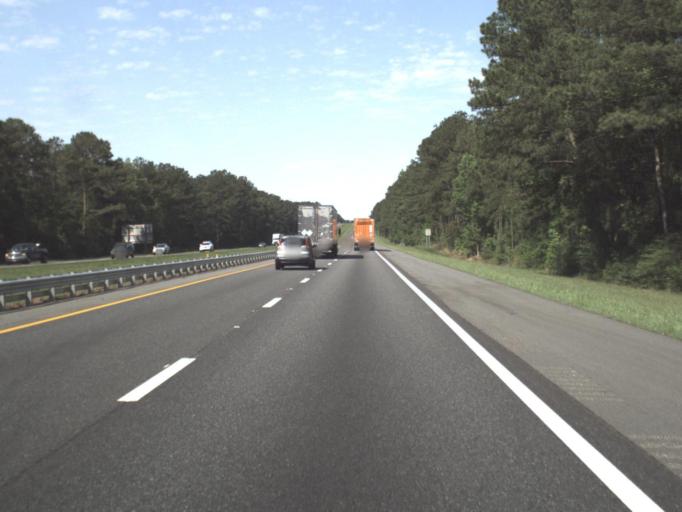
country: US
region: Florida
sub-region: Walton County
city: DeFuniak Springs
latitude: 30.7099
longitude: -85.9444
